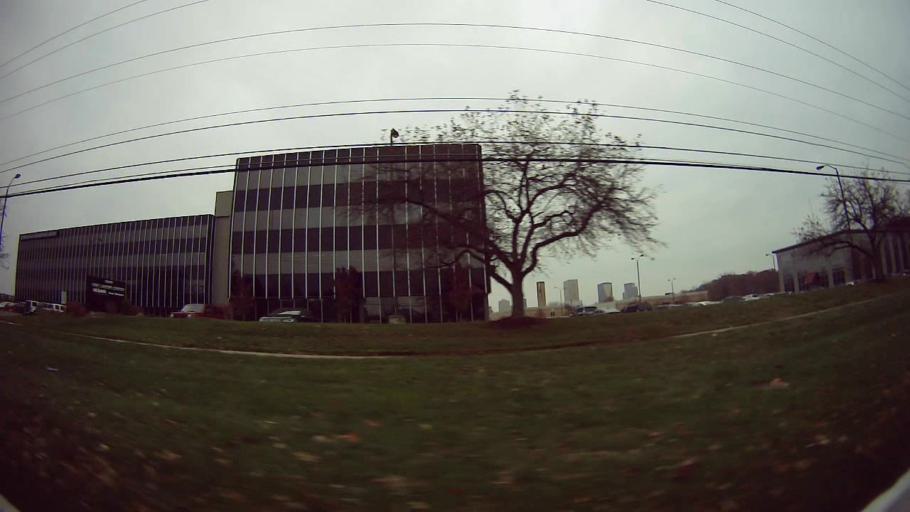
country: US
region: Michigan
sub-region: Oakland County
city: Bingham Farms
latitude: 42.4813
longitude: -83.2610
